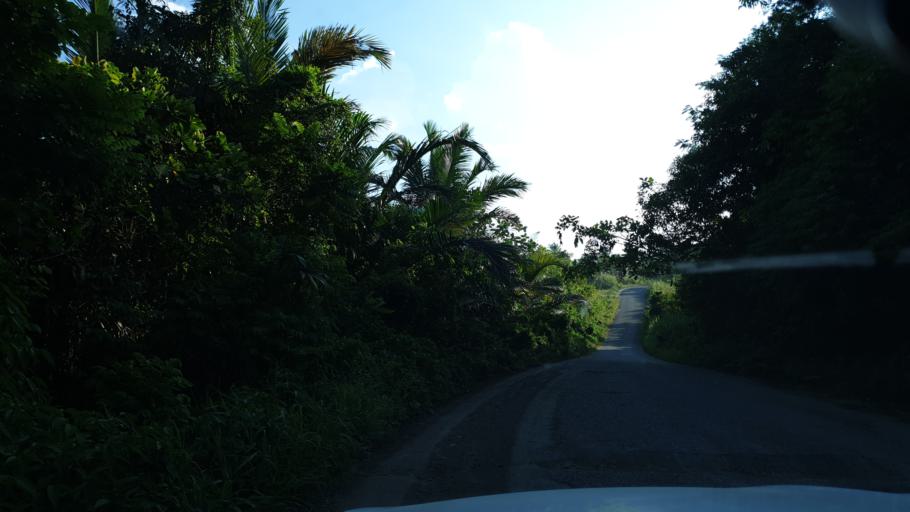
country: PG
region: East Sepik
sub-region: Wewak
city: Wewak
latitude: -3.6947
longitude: 143.6516
